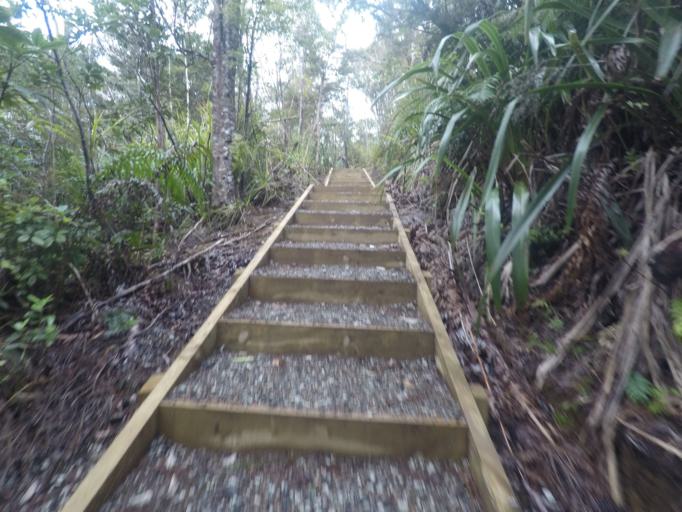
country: NZ
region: Auckland
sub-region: Auckland
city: Titirangi
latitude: -37.0013
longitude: 174.5395
